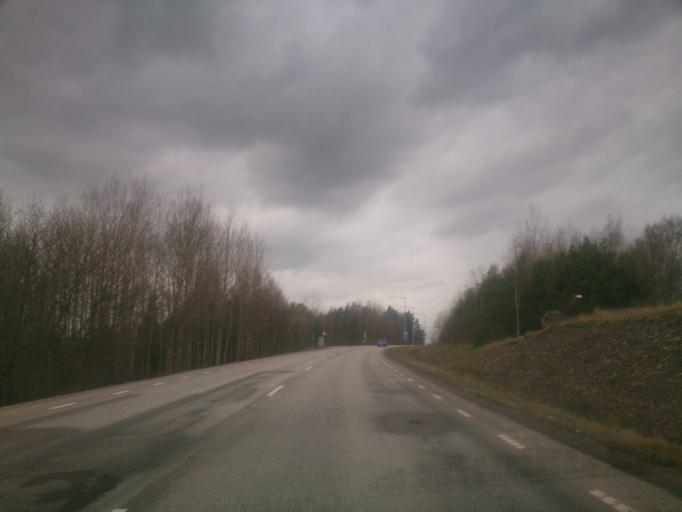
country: SE
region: OEstergoetland
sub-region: Norrkopings Kommun
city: Svartinge
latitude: 58.5717
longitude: 16.0646
